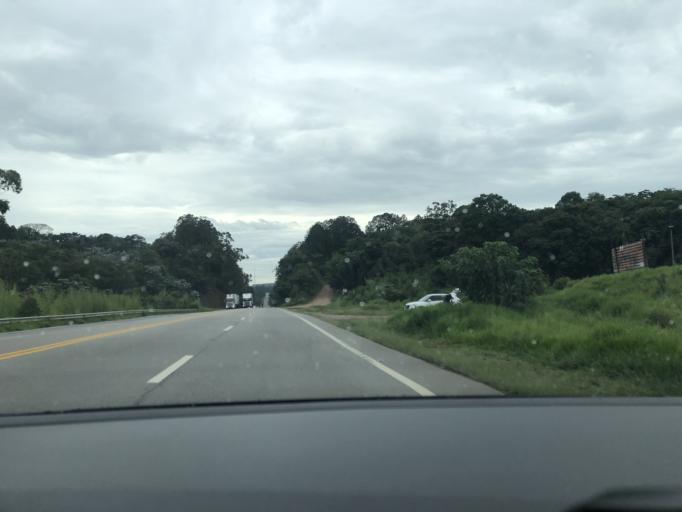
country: BR
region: Sao Paulo
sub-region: Campo Limpo Paulista
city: Campo Limpo Paulista
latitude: -23.1667
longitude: -46.7608
